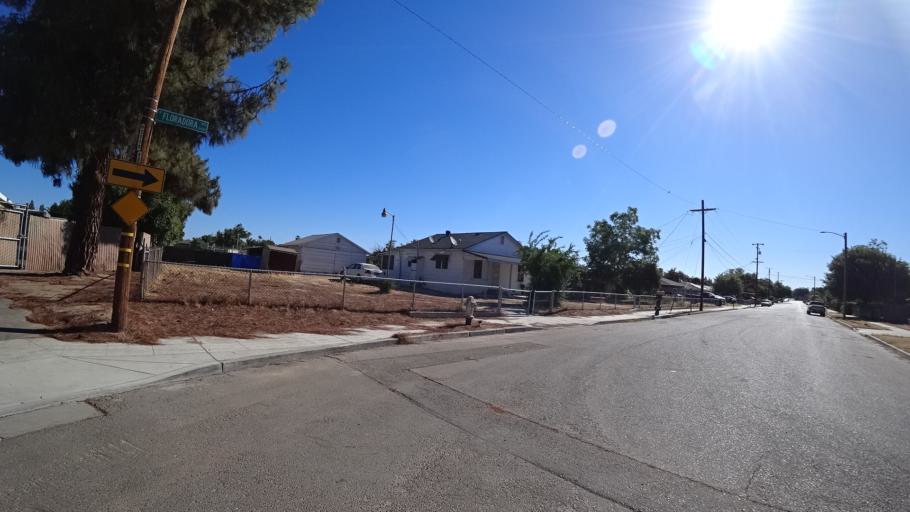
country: US
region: California
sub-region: Fresno County
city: West Park
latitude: 36.7611
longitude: -119.8399
